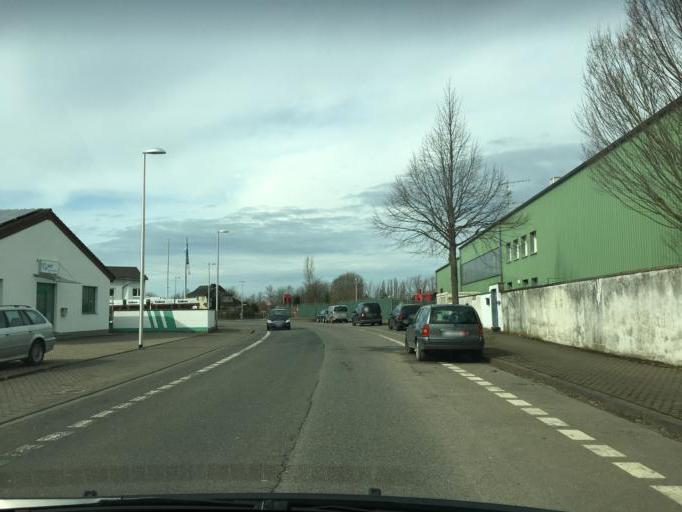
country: DE
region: North Rhine-Westphalia
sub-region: Regierungsbezirk Koln
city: Dueren
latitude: 50.8172
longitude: 6.5026
